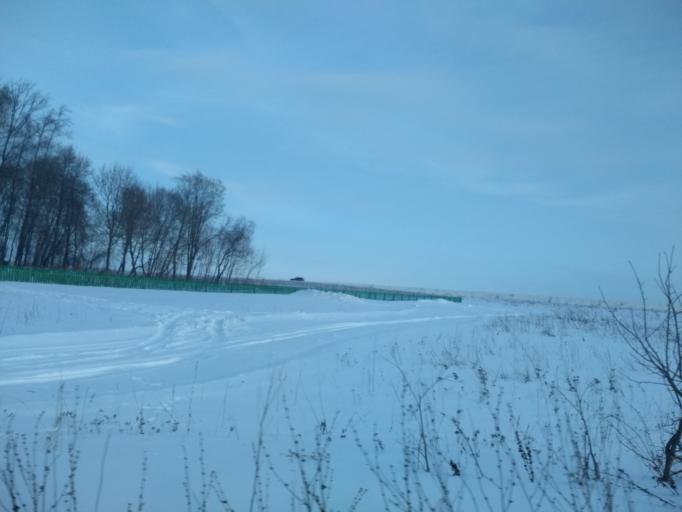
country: RU
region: Bashkortostan
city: Iglino
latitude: 54.7710
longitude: 56.5485
